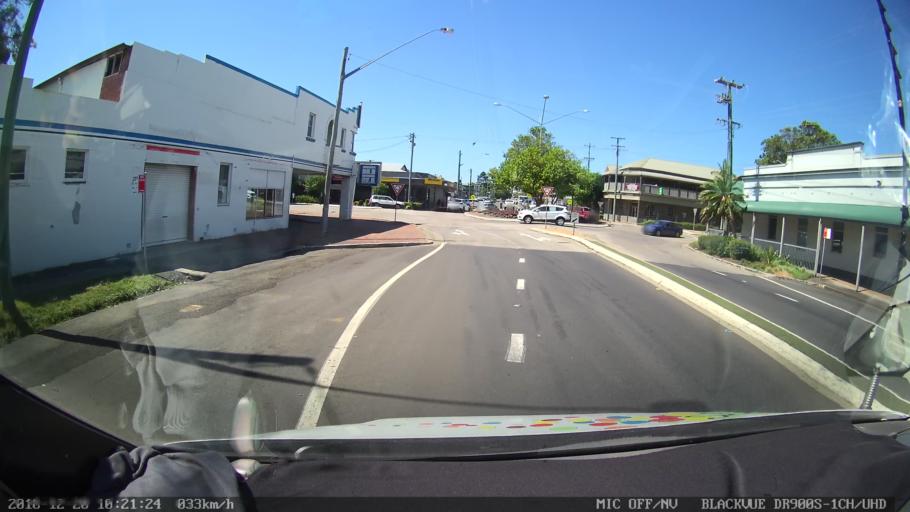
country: AU
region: New South Wales
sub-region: Richmond Valley
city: Casino
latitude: -28.8640
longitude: 153.0457
